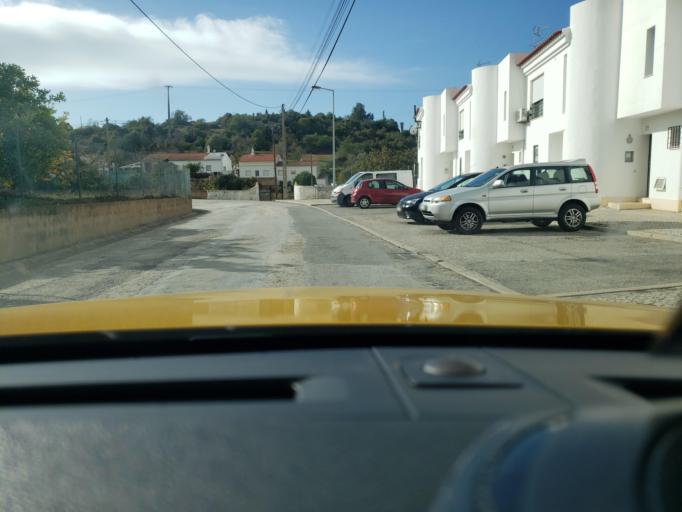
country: PT
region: Faro
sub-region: Lagoa
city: Carvoeiro
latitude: 37.1099
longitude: -8.4562
